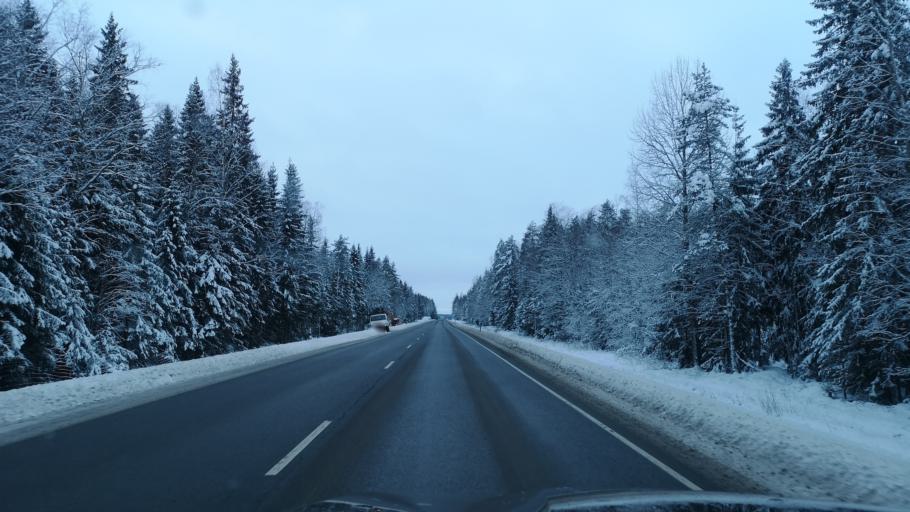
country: FI
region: Varsinais-Suomi
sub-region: Loimaa
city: Loimaa
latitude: 60.9028
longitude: 23.1445
